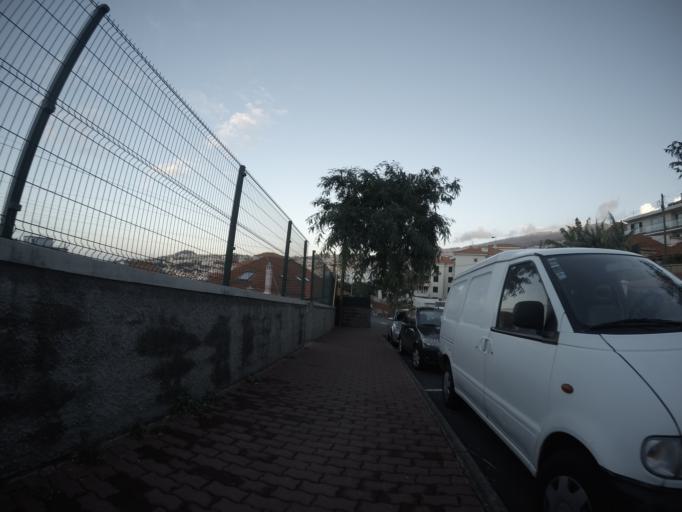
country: PT
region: Madeira
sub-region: Funchal
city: Nossa Senhora do Monte
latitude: 32.6500
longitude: -16.8974
